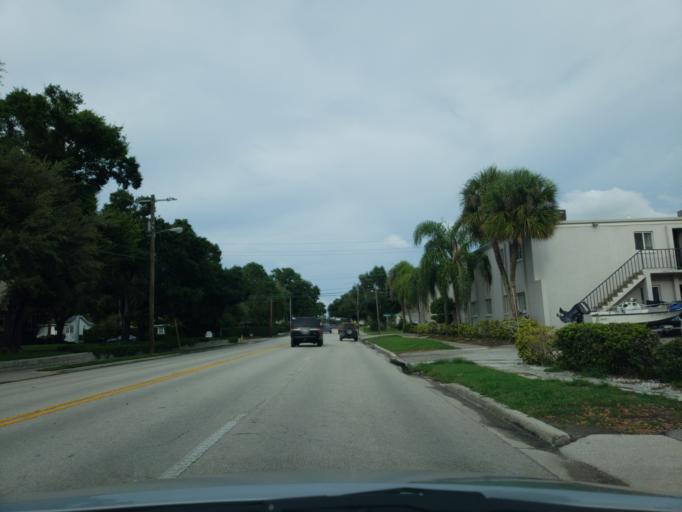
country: US
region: Florida
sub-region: Hillsborough County
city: Tampa
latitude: 27.9411
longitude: -82.4962
